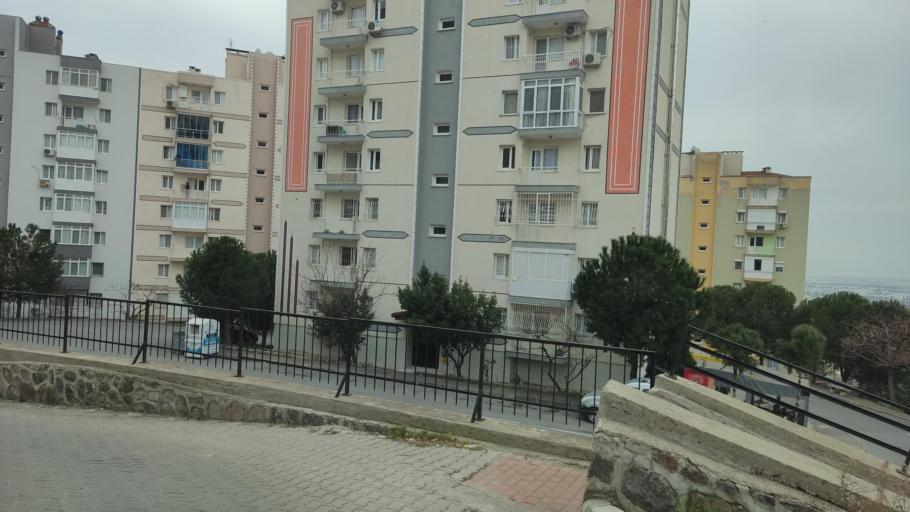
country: TR
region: Izmir
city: Karsiyaka
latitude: 38.5042
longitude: 27.0712
